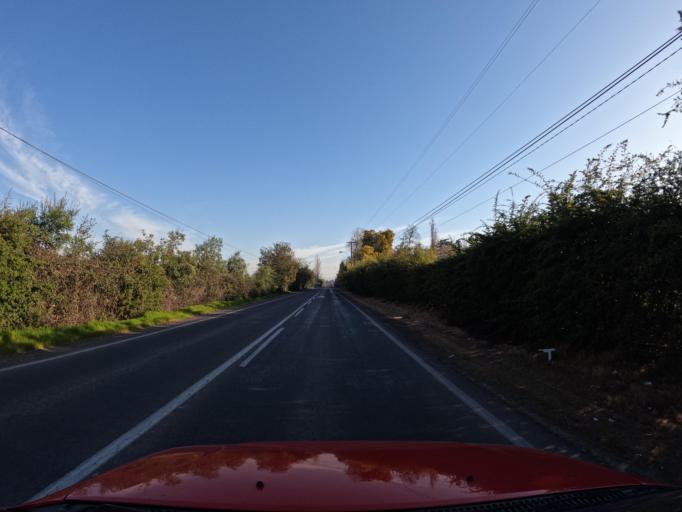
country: CL
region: Maule
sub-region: Provincia de Curico
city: Rauco
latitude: -34.9027
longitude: -71.2768
